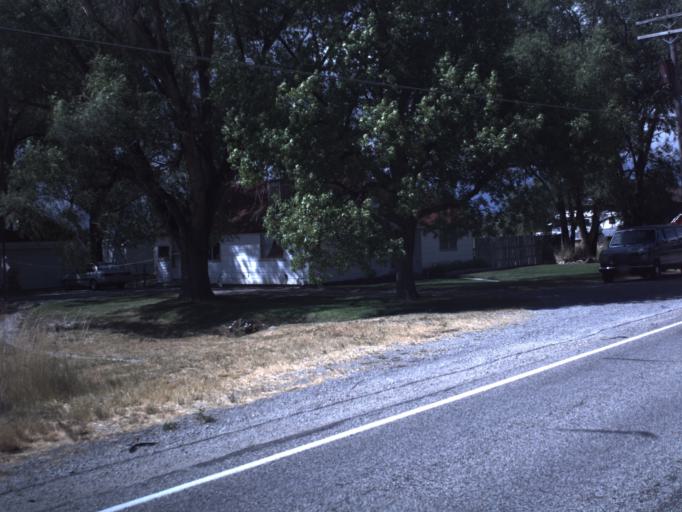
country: US
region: Utah
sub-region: Box Elder County
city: Honeyville
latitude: 41.6829
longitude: -112.0899
